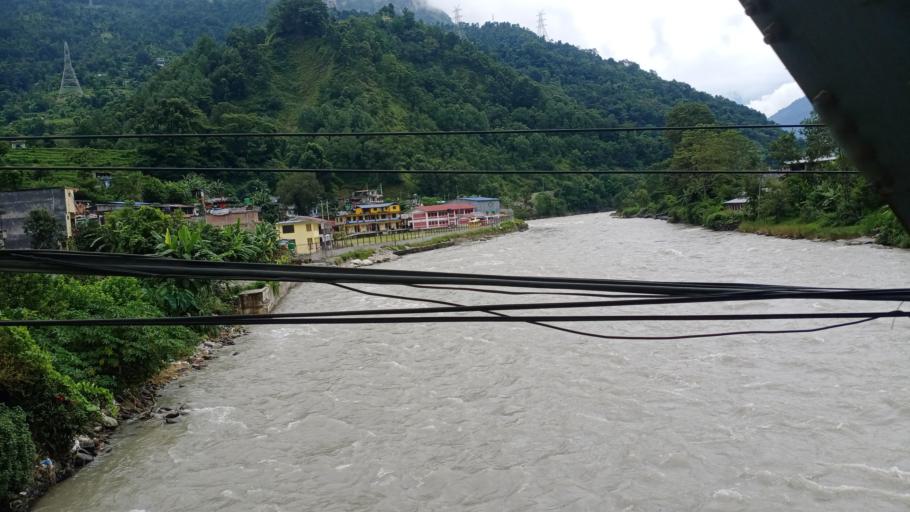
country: NP
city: Kodari
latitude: 27.7541
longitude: 85.8273
